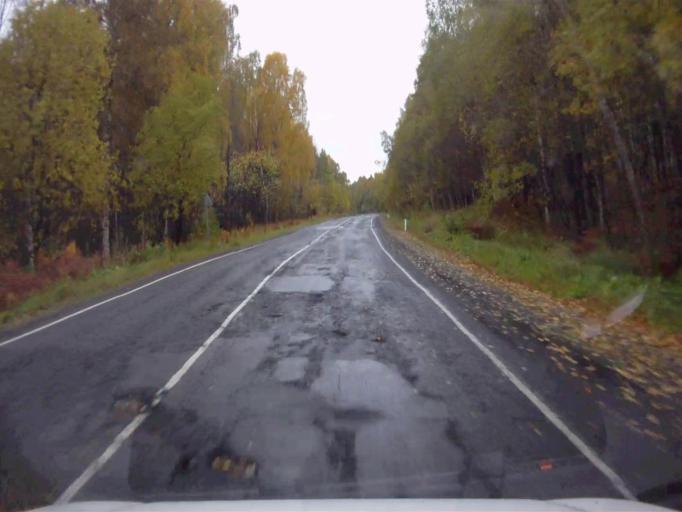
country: RU
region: Chelyabinsk
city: Nizhniy Ufaley
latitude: 56.0542
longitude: 60.0561
